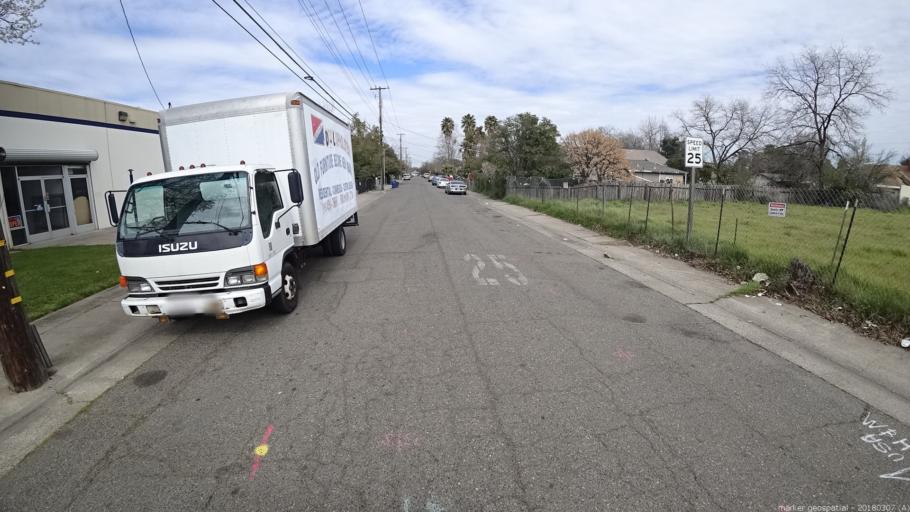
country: US
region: California
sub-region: Sacramento County
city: Parkway
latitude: 38.5251
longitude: -121.4600
